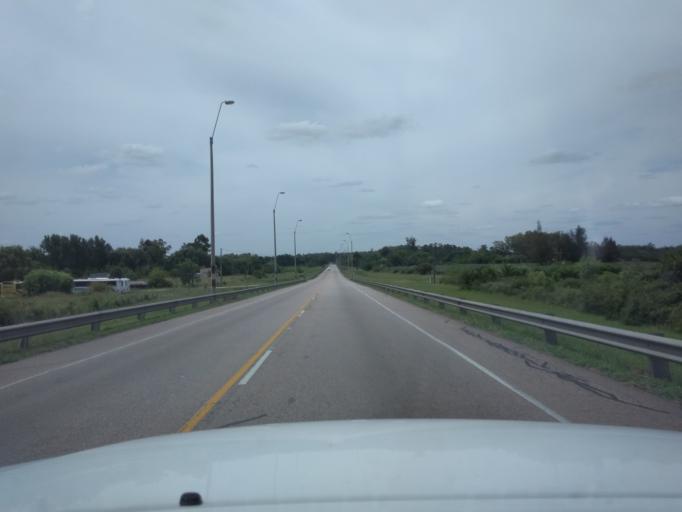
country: UY
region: Canelones
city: Canelones
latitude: -34.5411
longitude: -56.2739
